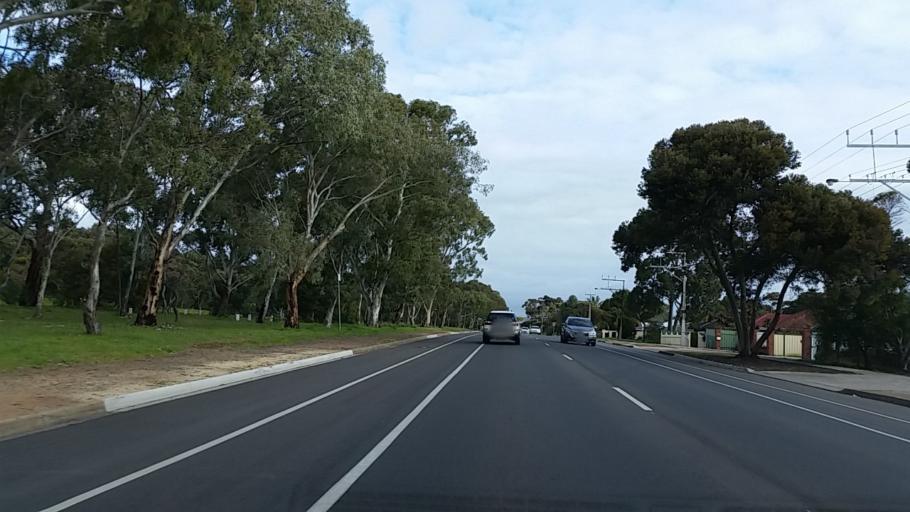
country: AU
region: South Australia
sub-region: Onkaparinga
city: Morphett Vale
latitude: -35.1231
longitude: 138.5362
